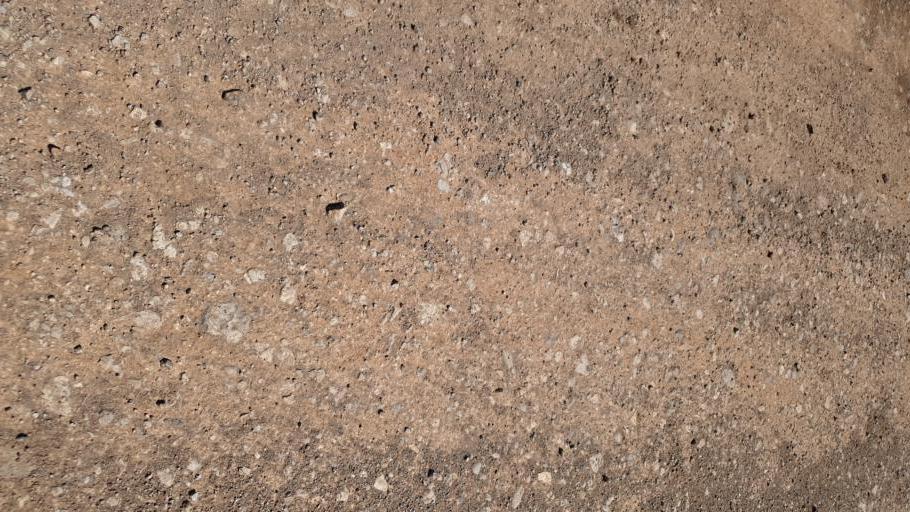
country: ET
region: Oromiya
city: Fiche
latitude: 9.6394
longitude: 38.9707
